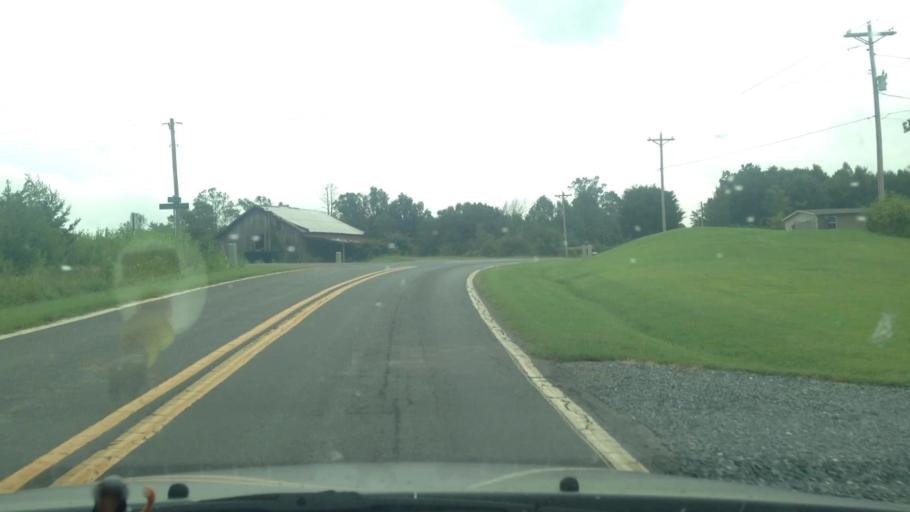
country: US
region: North Carolina
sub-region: Stokes County
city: Danbury
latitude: 36.3898
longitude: -80.1367
